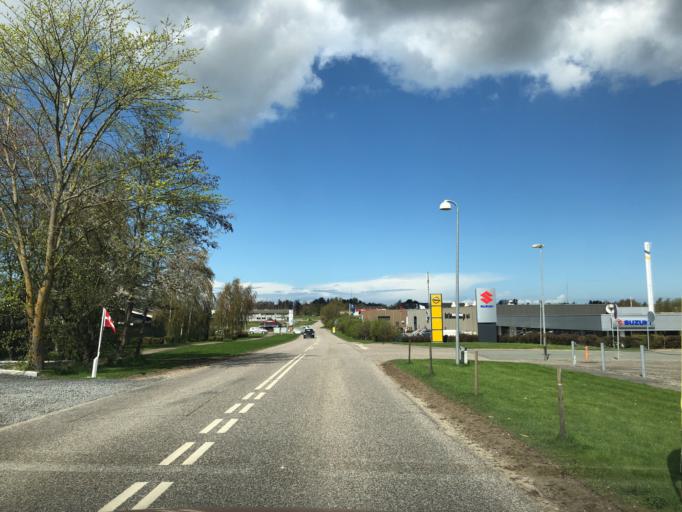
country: DK
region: Capital Region
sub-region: Gribskov Kommune
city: Helsinge
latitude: 56.0202
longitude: 12.1778
